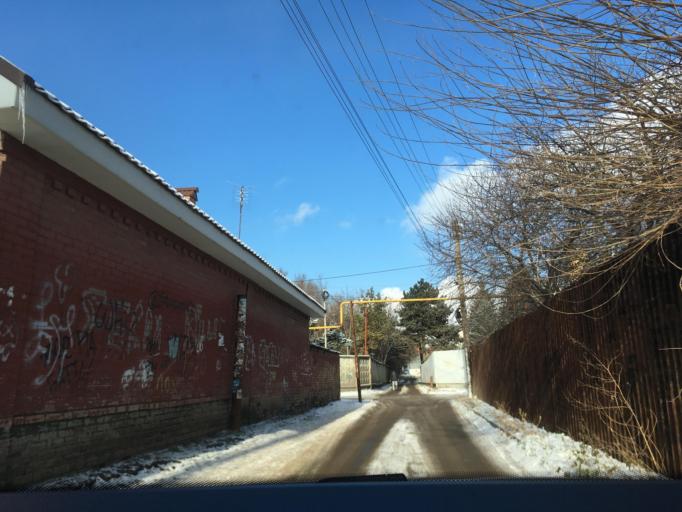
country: RU
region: Rostov
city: Rostov-na-Donu
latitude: 47.2360
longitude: 39.6295
